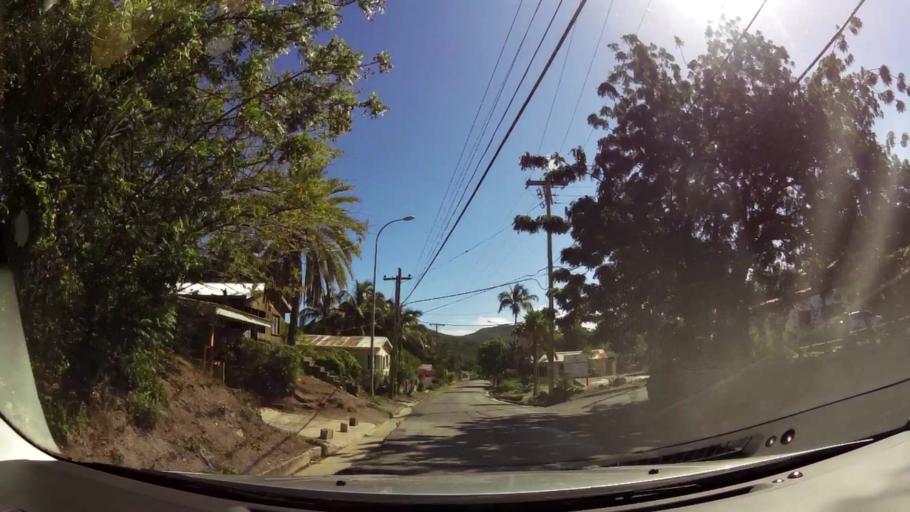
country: AG
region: Saint Paul
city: Falmouth
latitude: 17.0165
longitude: -61.7657
